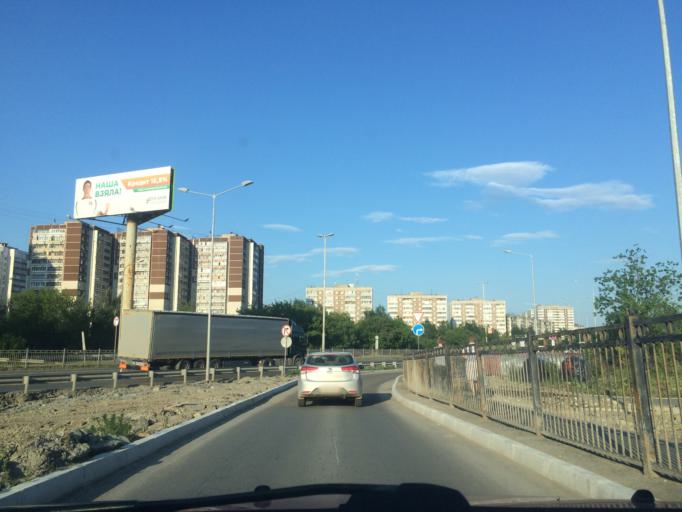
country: RU
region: Sverdlovsk
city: Yekaterinburg
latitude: 56.8288
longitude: 60.6772
